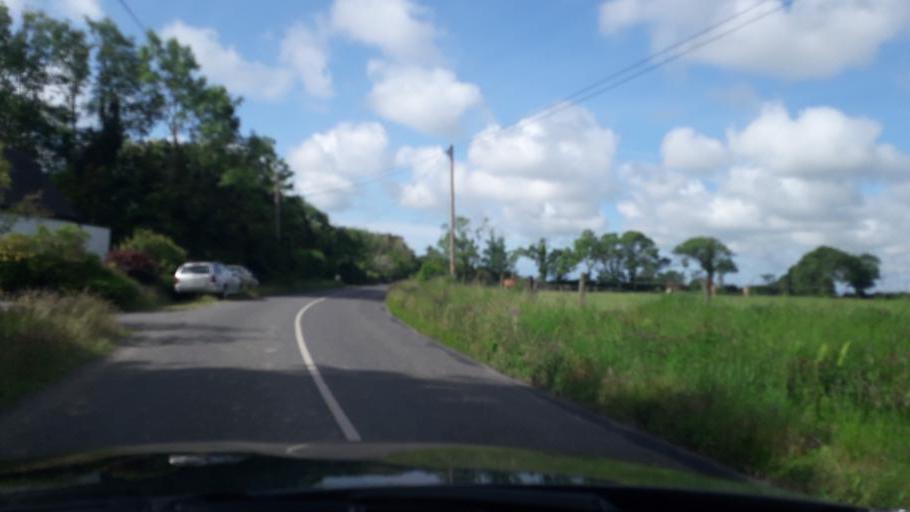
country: IE
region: Leinster
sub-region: Loch Garman
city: Loch Garman
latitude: 52.2796
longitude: -6.5404
